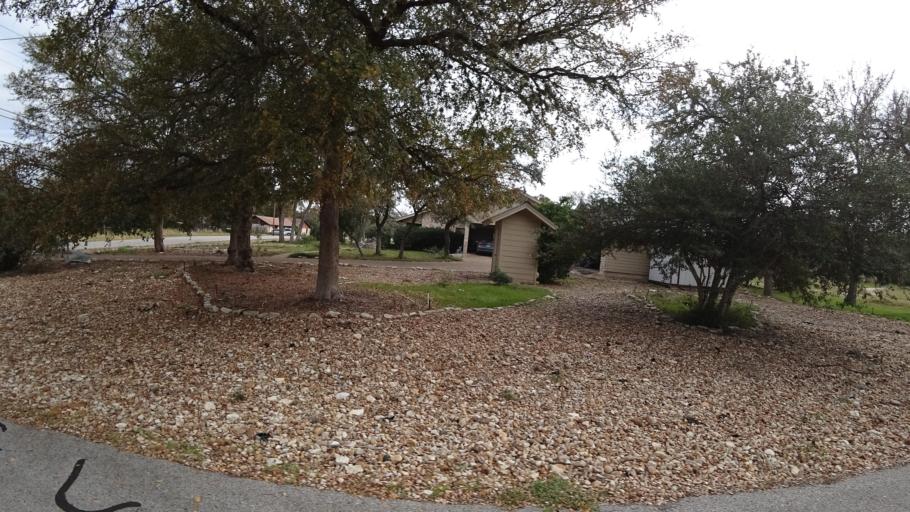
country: US
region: Texas
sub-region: Travis County
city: Shady Hollow
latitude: 30.1358
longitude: -97.8886
